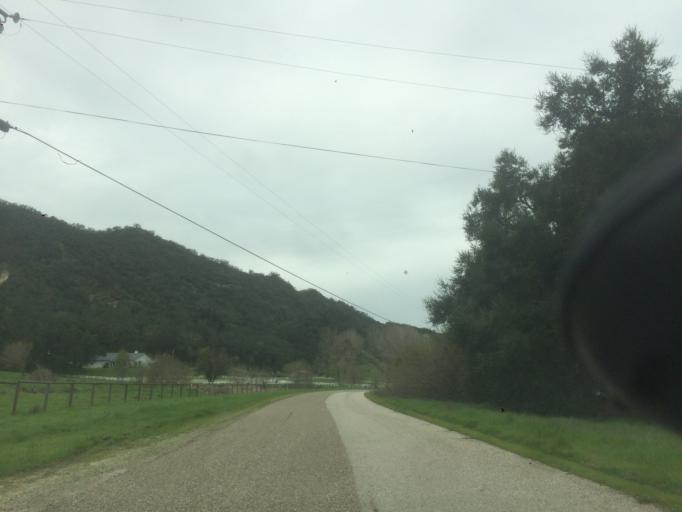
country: US
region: California
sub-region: San Luis Obispo County
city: Nipomo
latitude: 35.2065
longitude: -120.3967
